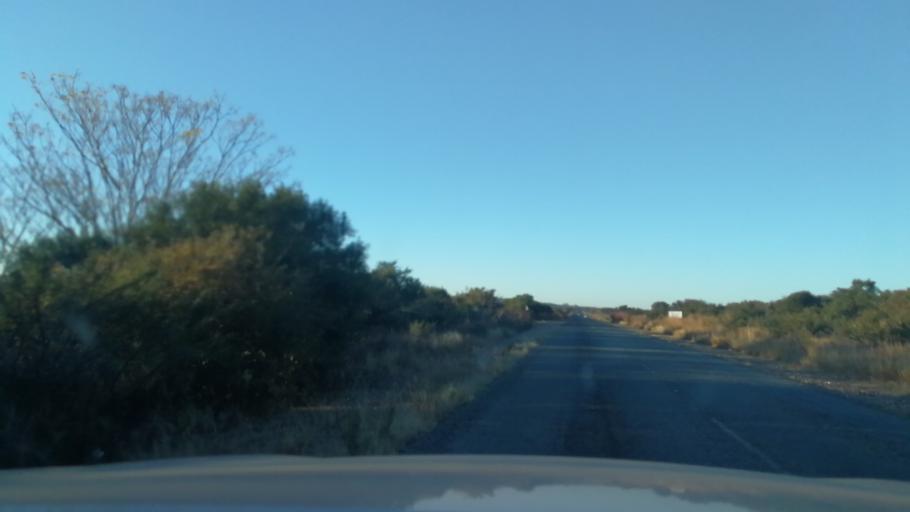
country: ZA
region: North-West
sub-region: Bojanala Platinum District Municipality
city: Koster
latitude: -25.7096
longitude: 26.7393
